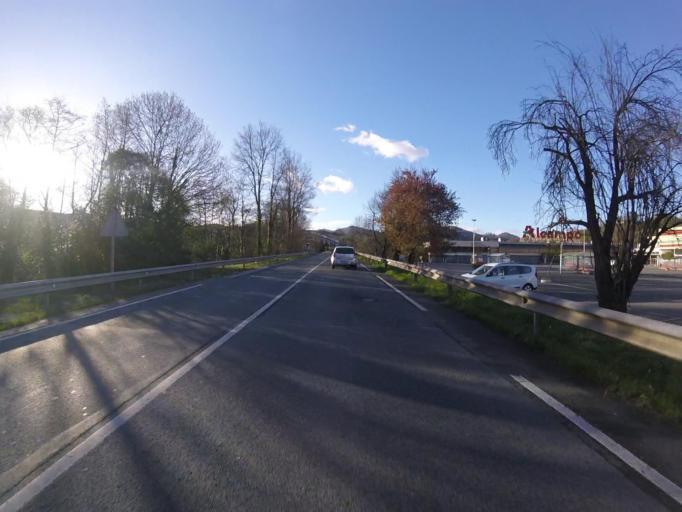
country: ES
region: Basque Country
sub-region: Provincia de Guipuzcoa
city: Errenteria
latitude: 43.3018
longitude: -1.8821
